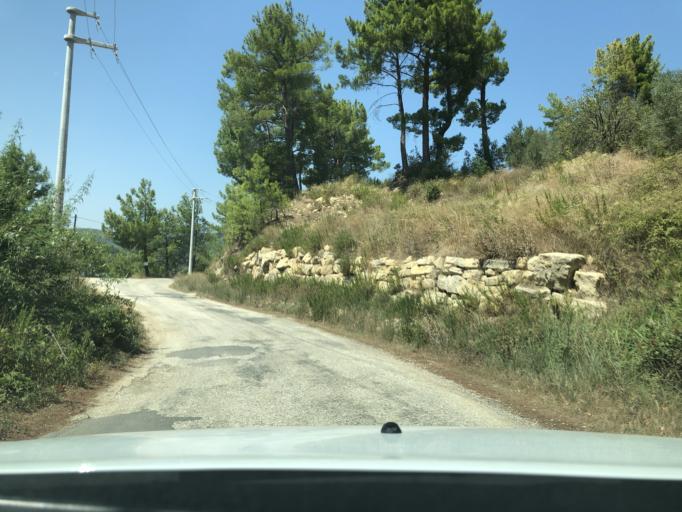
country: TR
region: Antalya
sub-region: Manavgat
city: Manavgat
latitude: 36.8718
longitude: 31.5524
